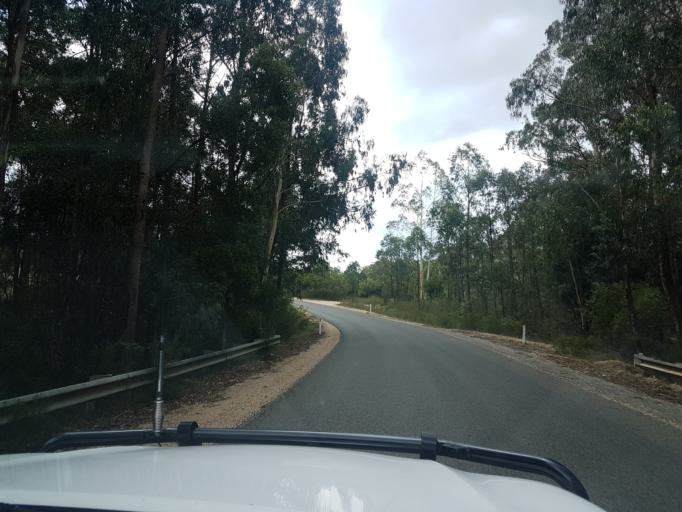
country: AU
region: Victoria
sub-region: East Gippsland
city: Bairnsdale
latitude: -37.6773
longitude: 147.5513
